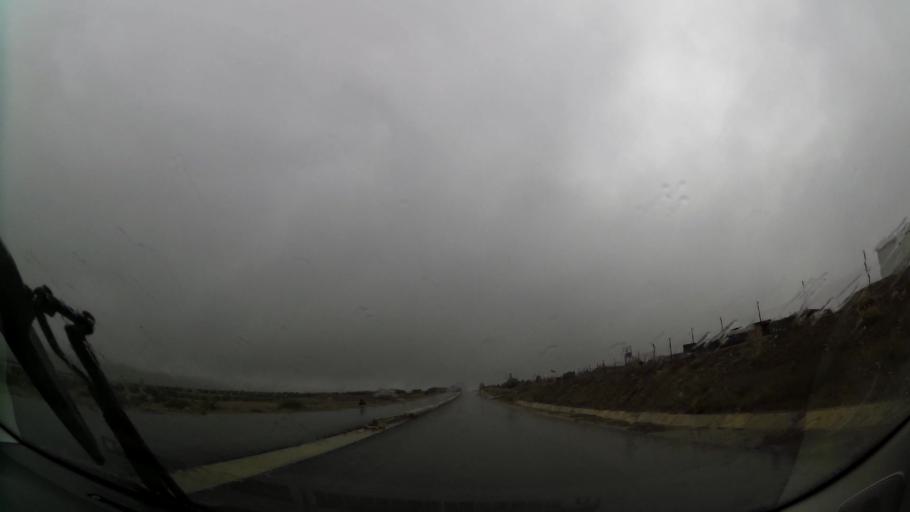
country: MA
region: Oriental
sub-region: Nador
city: Midar
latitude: 34.8640
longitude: -3.7239
